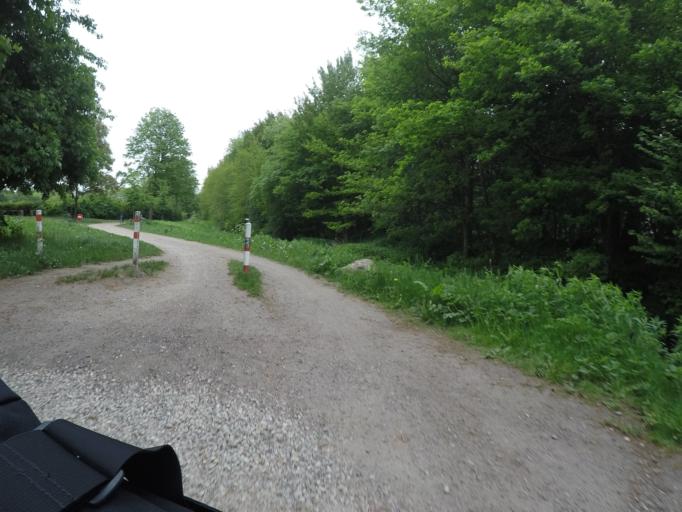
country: DE
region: Hamburg
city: Winterhude
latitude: 53.6289
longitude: 9.9793
